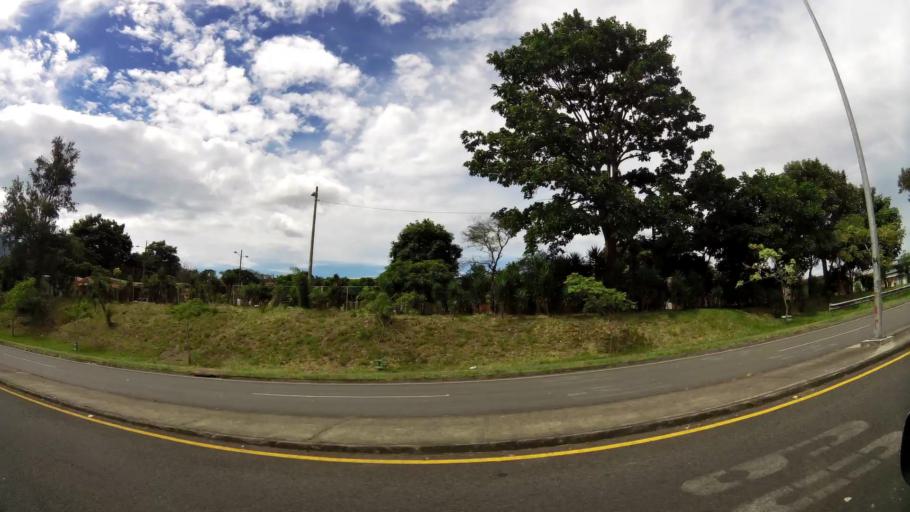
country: CR
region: San Jose
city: Alajuelita
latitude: 9.9079
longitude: -84.0748
